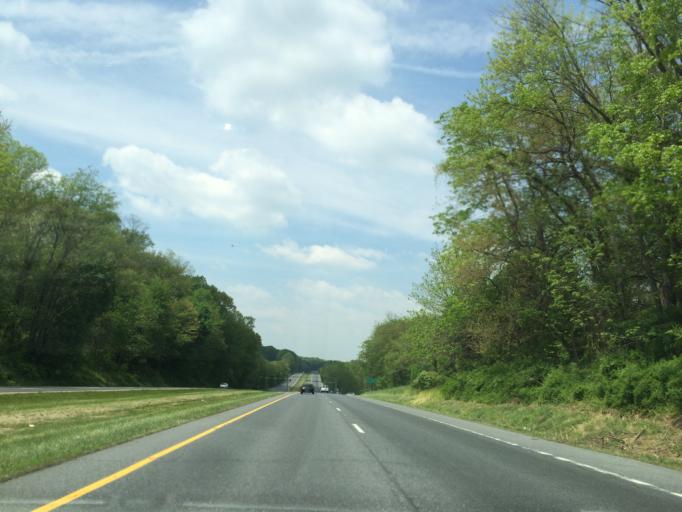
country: US
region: Maryland
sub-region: Howard County
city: Columbia
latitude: 39.2886
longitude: -76.8865
